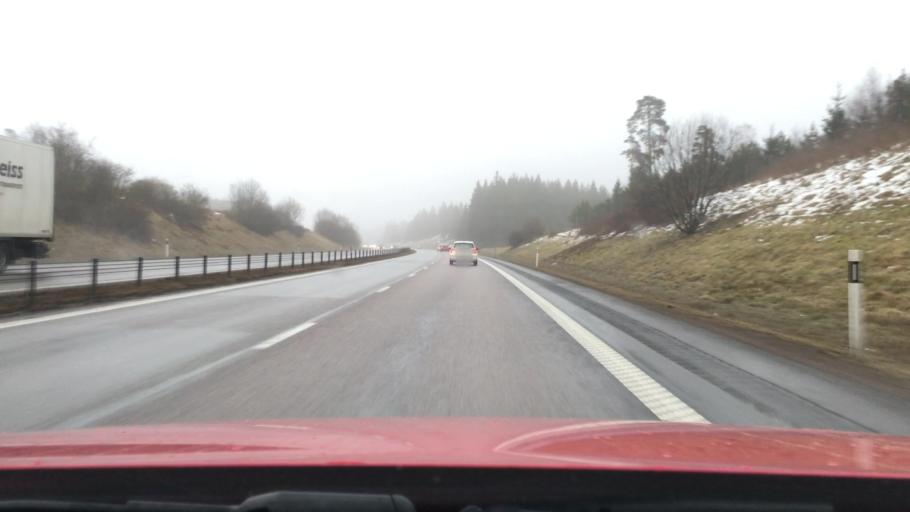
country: SE
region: Vaestra Goetaland
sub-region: Trollhattan
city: Sjuntorp
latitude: 58.3287
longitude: 12.1380
